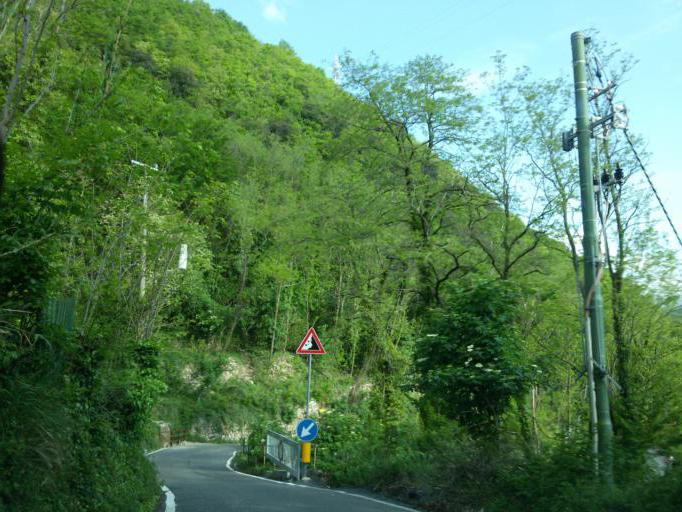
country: IT
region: Liguria
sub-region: Provincia di Genova
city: Piccarello
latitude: 44.4466
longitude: 8.9897
